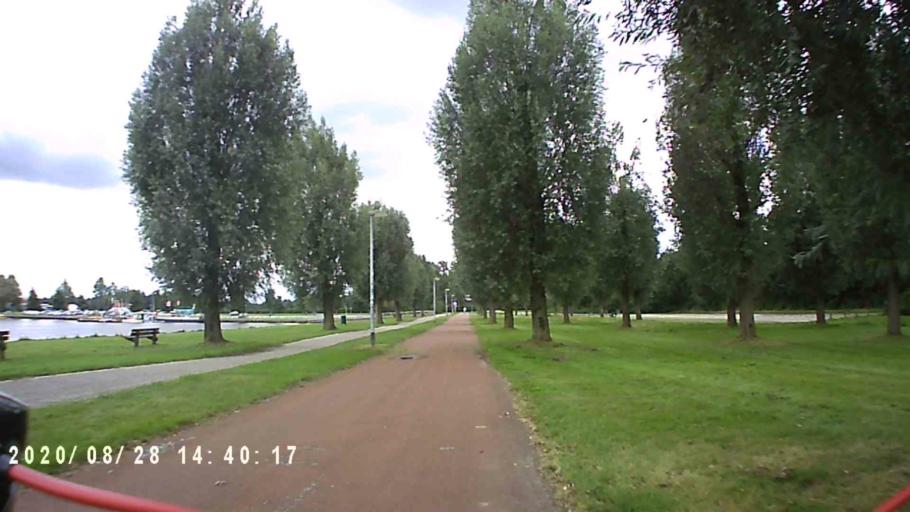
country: NL
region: Groningen
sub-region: Gemeente Groningen
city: Groningen
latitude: 53.1819
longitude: 6.5535
